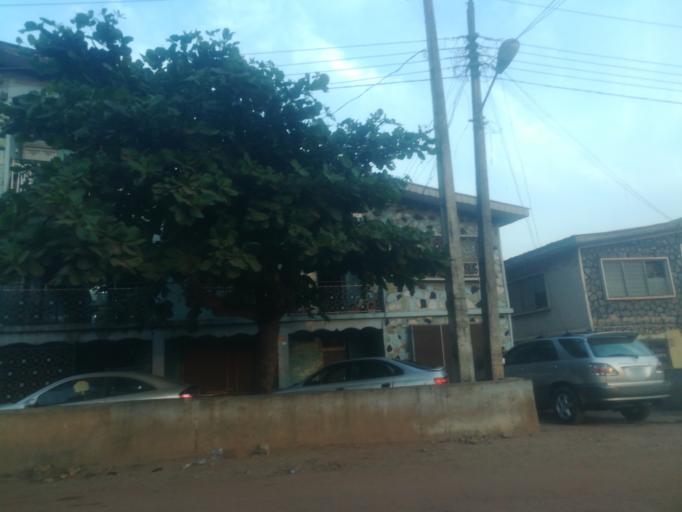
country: NG
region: Ogun
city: Abeokuta
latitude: 7.1474
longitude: 3.3389
